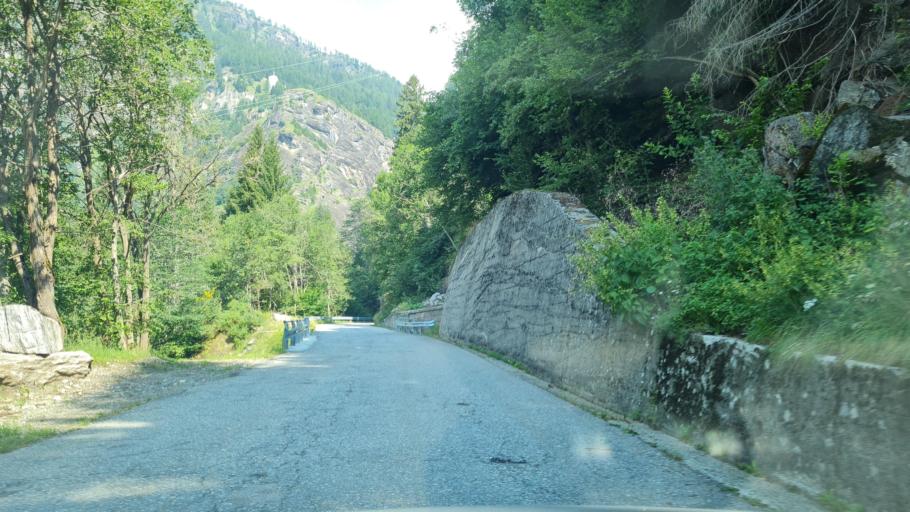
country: IT
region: Piedmont
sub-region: Provincia Verbano-Cusio-Ossola
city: Baceno
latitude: 46.2973
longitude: 8.2692
